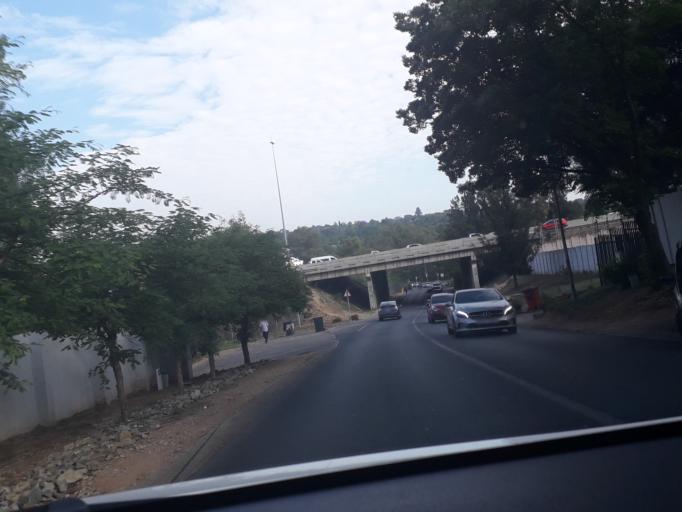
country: ZA
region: Gauteng
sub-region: City of Johannesburg Metropolitan Municipality
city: Diepsloot
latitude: -26.0623
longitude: 27.9842
